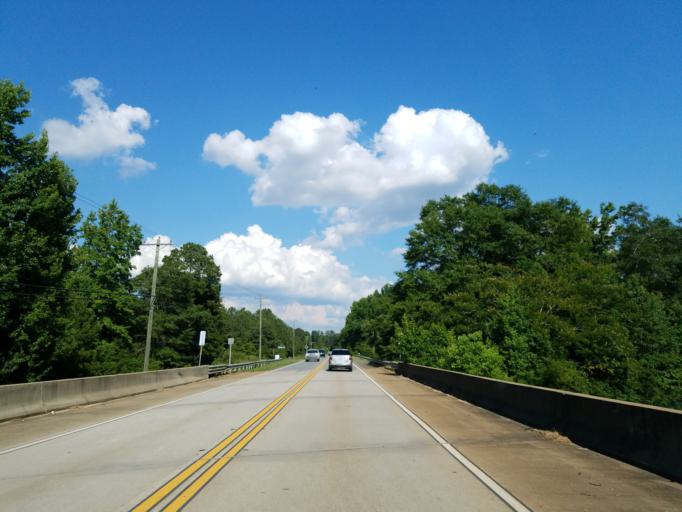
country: US
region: Georgia
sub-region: Houston County
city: Perry
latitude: 32.5482
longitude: -83.7642
